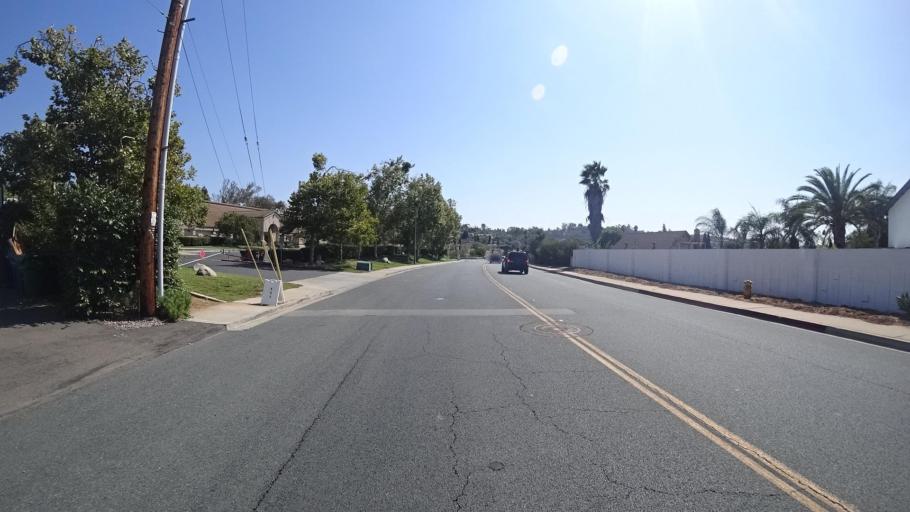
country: US
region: California
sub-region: San Diego County
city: Granite Hills
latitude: 32.7886
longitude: -116.9179
